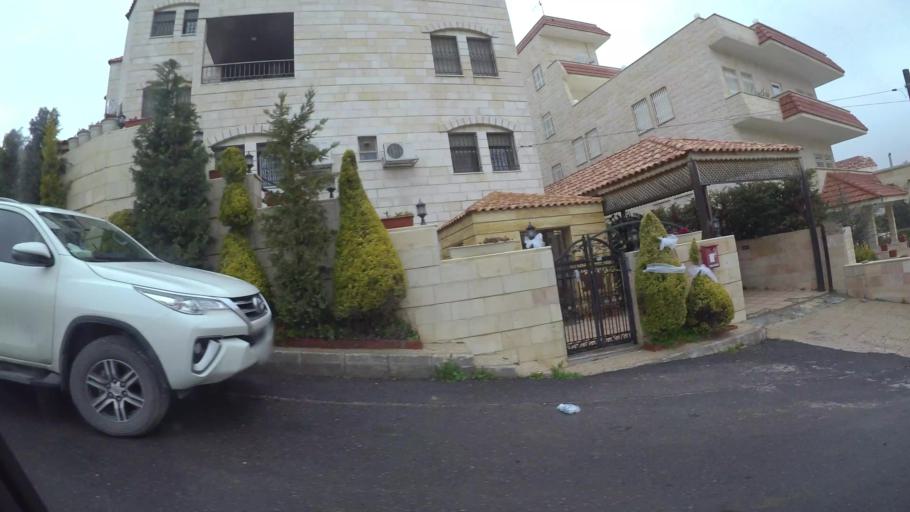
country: JO
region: Amman
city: Al Jubayhah
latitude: 32.0110
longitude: 35.8303
